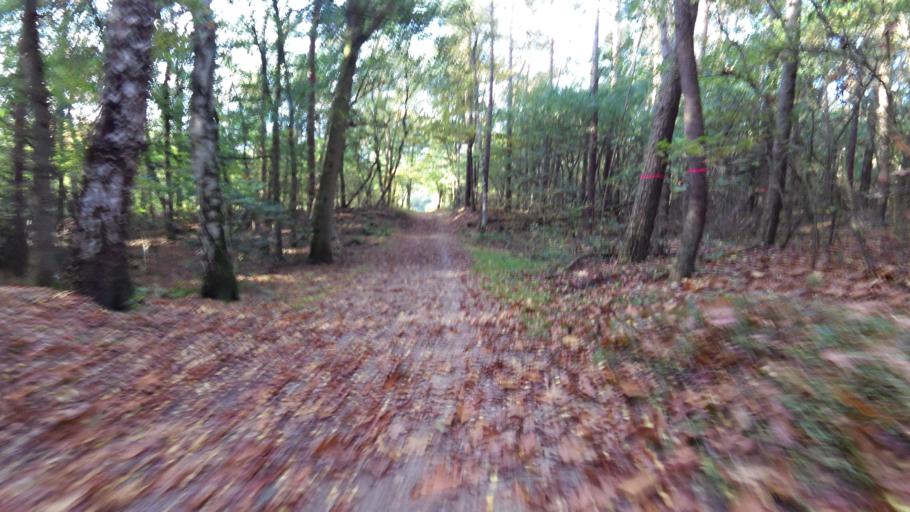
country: NL
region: Gelderland
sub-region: Gemeente Ede
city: Ede
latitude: 52.0575
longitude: 5.6647
